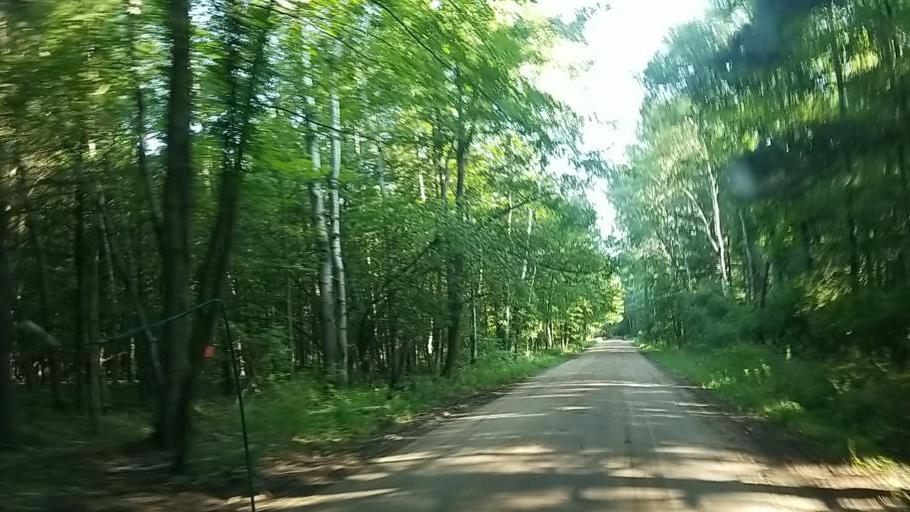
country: US
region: Michigan
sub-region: Newaygo County
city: Newaygo
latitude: 43.3750
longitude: -85.8504
